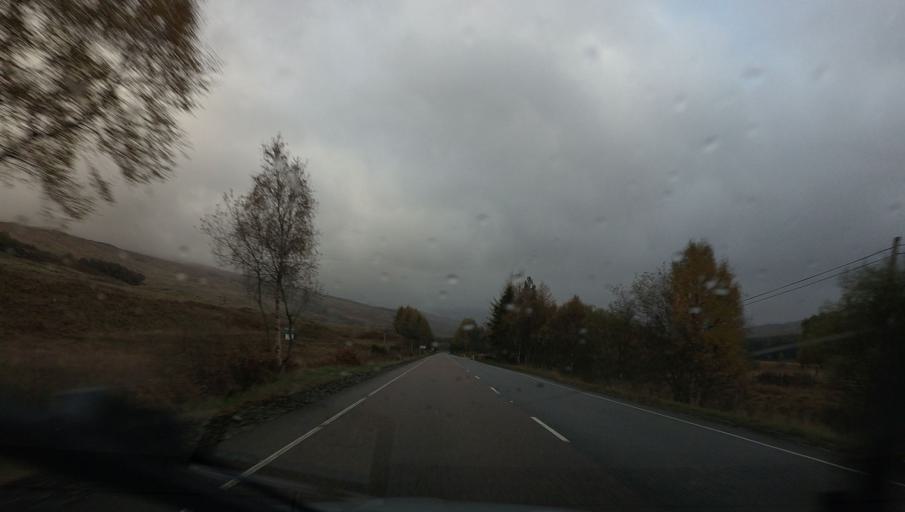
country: GB
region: Scotland
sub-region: Argyll and Bute
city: Garelochhead
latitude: 56.4264
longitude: -4.6891
